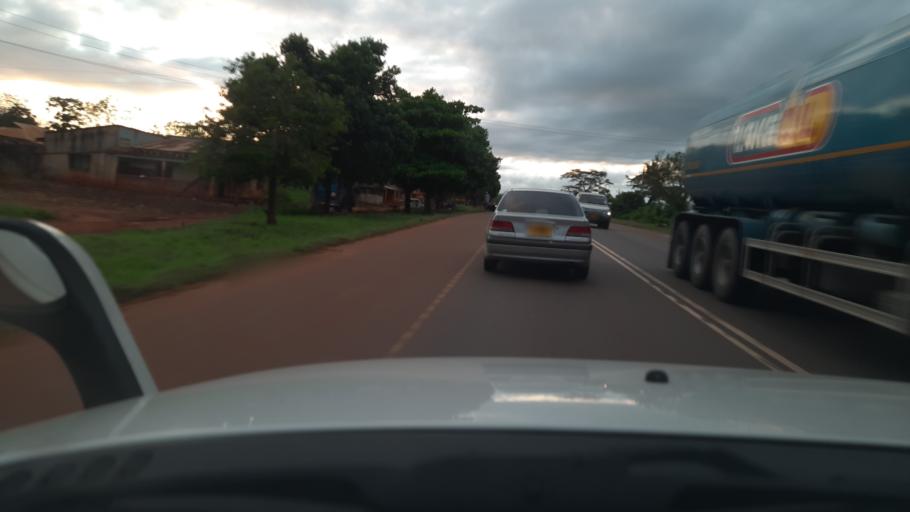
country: TZ
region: Tanga
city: Muheza
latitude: -5.1391
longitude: 38.8729
